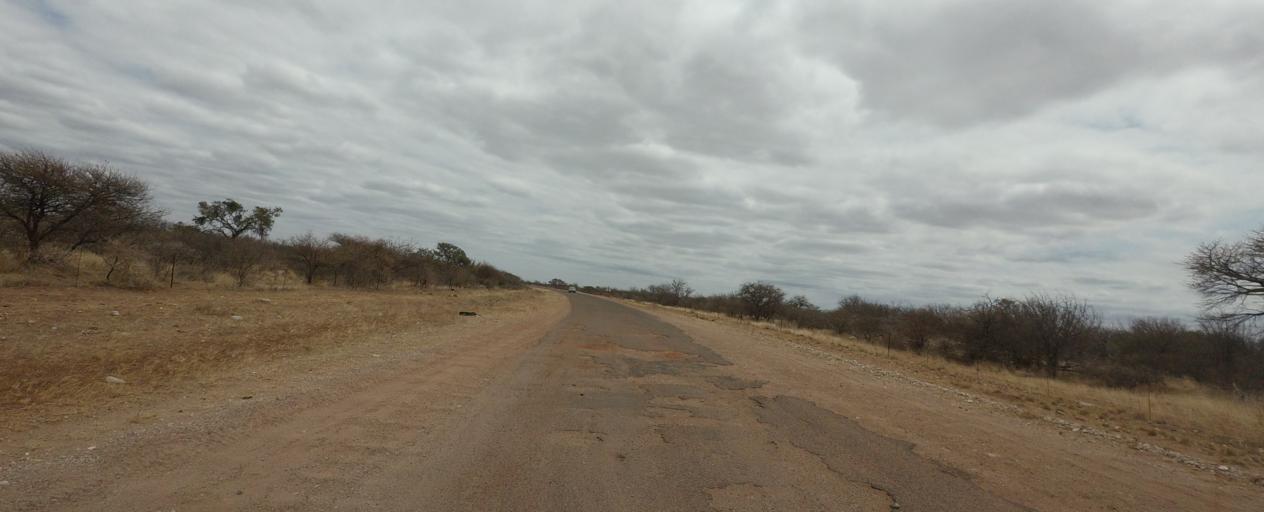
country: BW
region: Central
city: Makobeng
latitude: -22.8326
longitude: 28.2150
